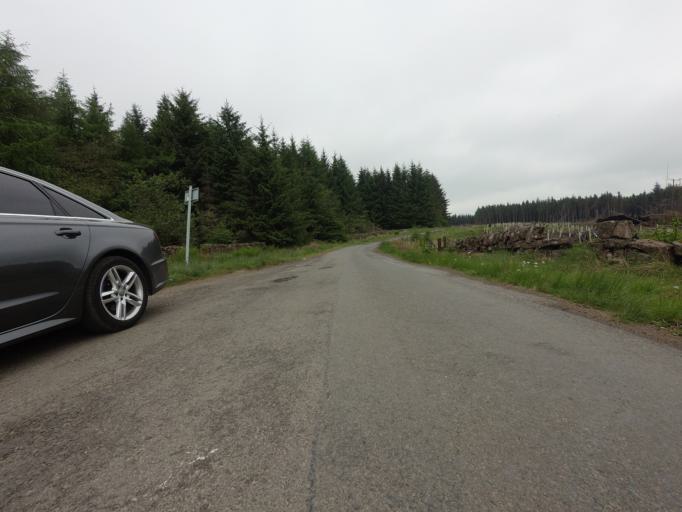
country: GB
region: Scotland
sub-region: Fife
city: Townhill
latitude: 56.1423
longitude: -3.4496
